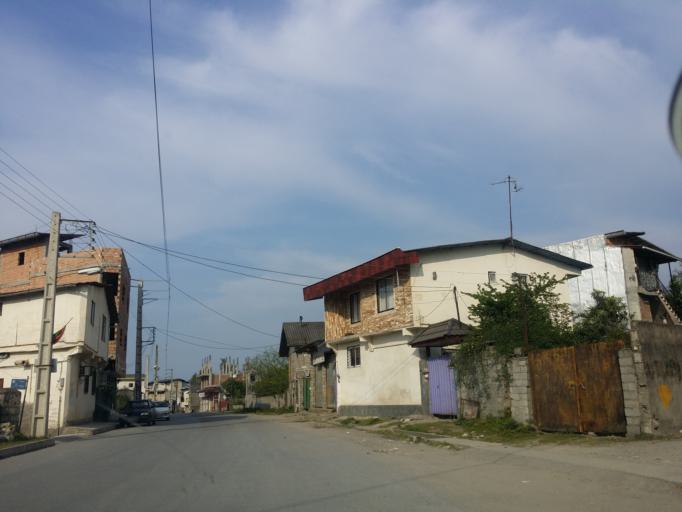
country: IR
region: Mazandaran
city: Chalus
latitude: 36.6581
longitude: 51.3968
